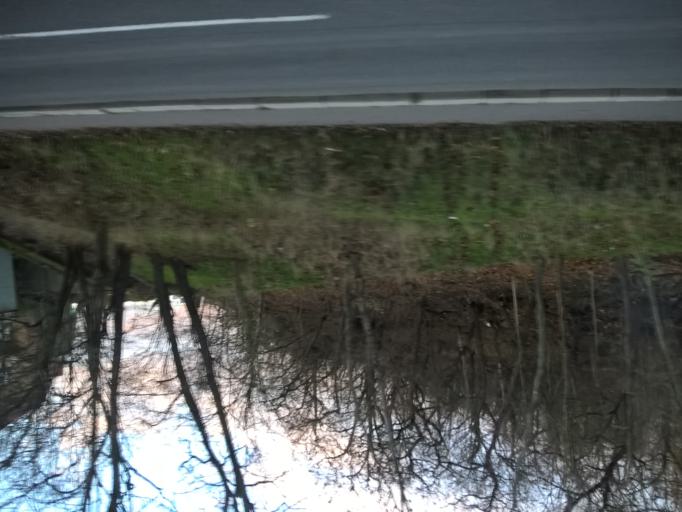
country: CZ
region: Praha
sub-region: Praha 1
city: Mala Strana
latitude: 50.0722
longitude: 14.3801
